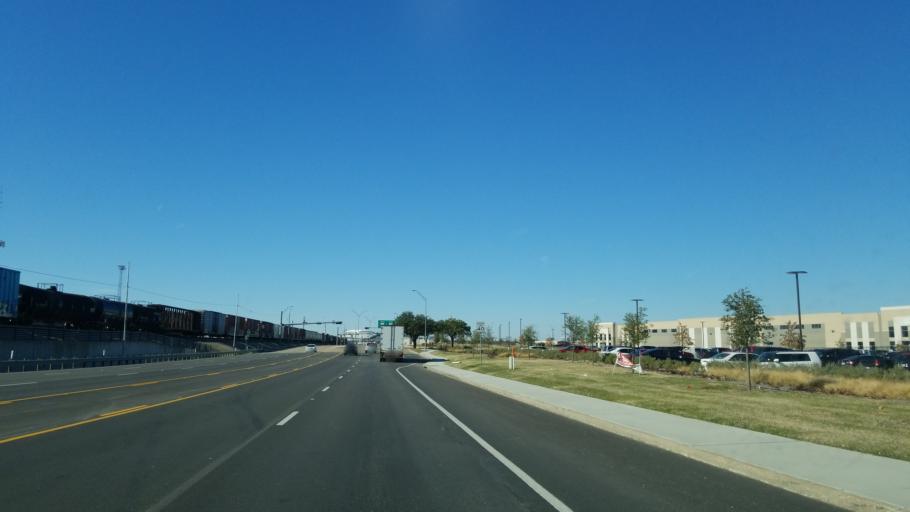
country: US
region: Texas
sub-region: Tarrant County
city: Arlington
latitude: 32.7416
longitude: -97.0563
